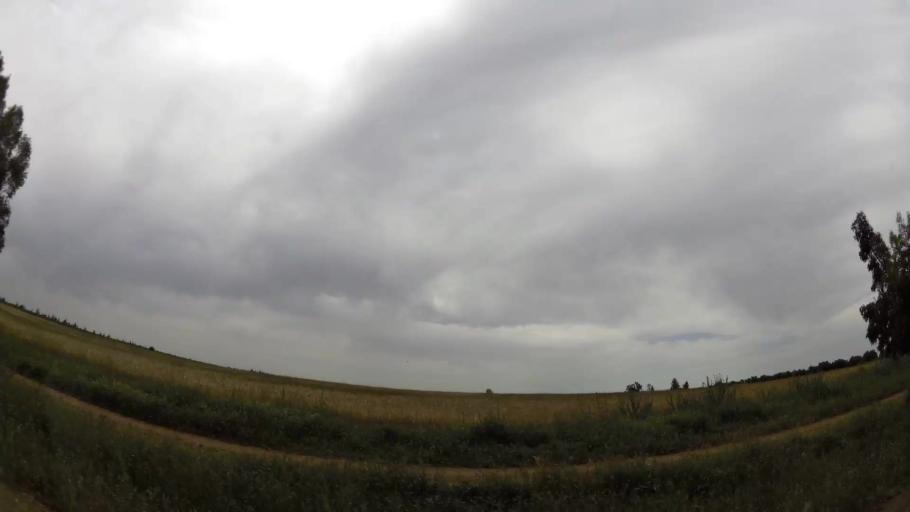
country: MA
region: Rabat-Sale-Zemmour-Zaer
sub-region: Khemisset
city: Tiflet
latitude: 33.8118
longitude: -6.2726
